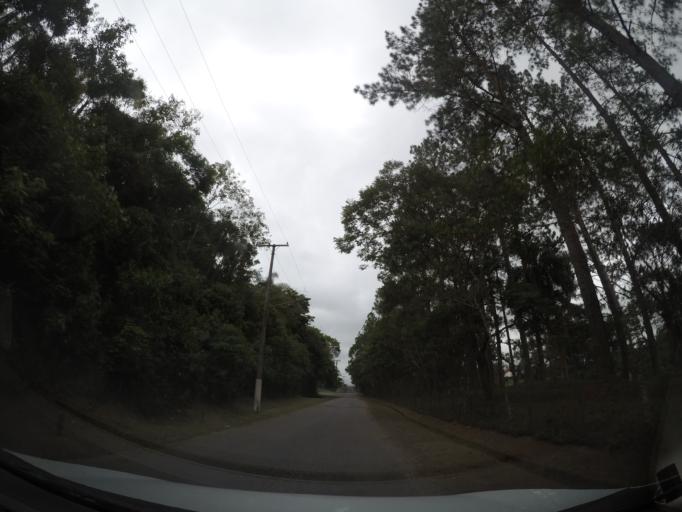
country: BR
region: Sao Paulo
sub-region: Aruja
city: Aruja
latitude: -23.3728
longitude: -46.3654
